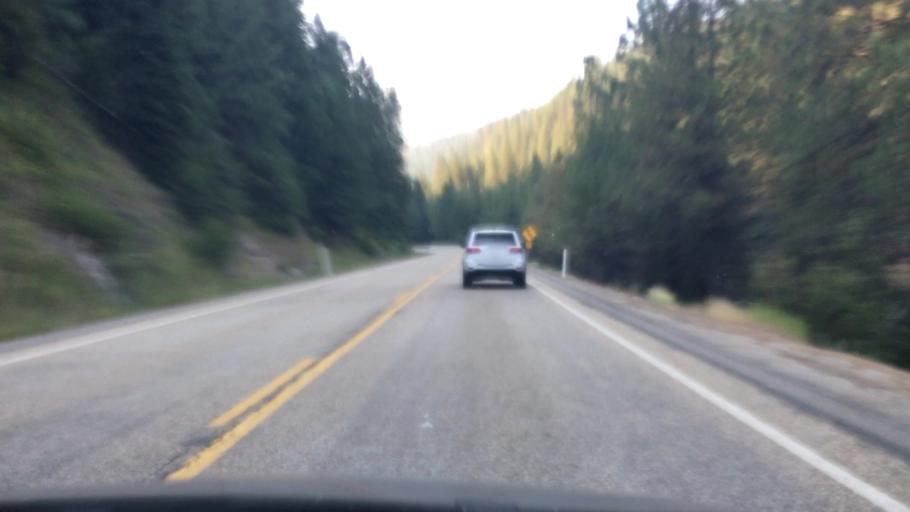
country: US
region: Idaho
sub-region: Valley County
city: Cascade
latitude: 44.2022
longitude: -116.1106
